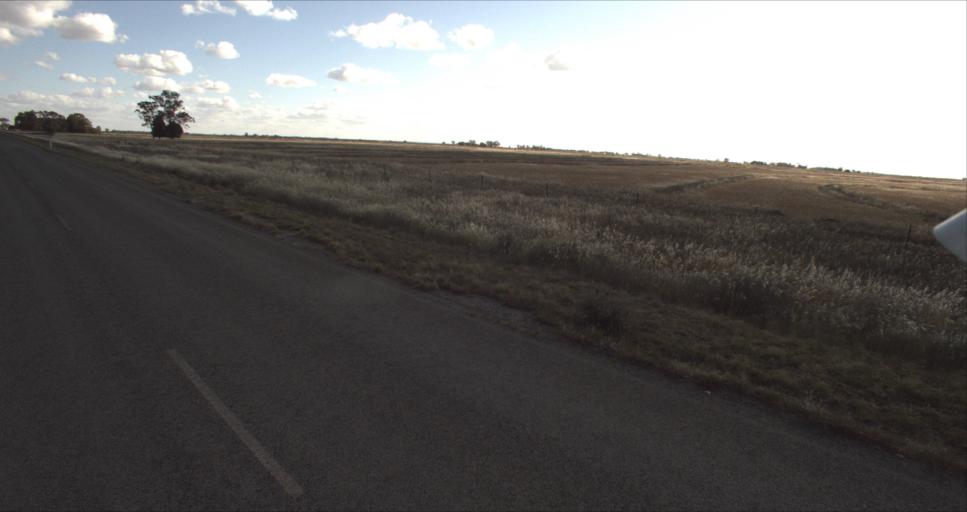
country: AU
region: New South Wales
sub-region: Leeton
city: Leeton
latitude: -34.5328
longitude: 146.2811
